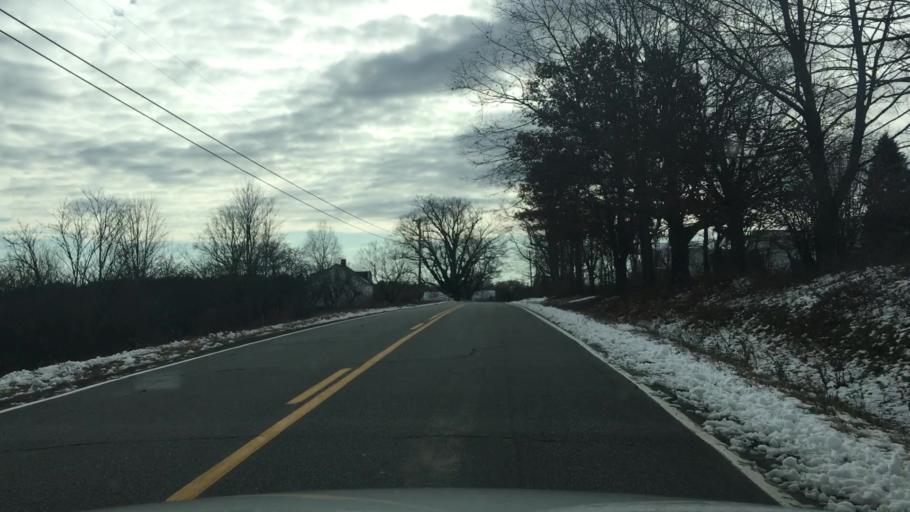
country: US
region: Maine
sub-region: Androscoggin County
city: Livermore
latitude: 44.3785
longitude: -70.2063
